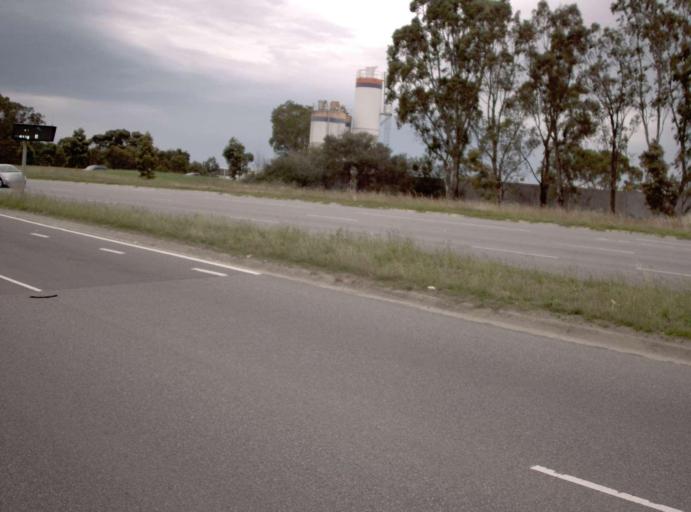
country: AU
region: Victoria
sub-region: Casey
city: Hampton Park
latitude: -38.0347
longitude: 145.2455
